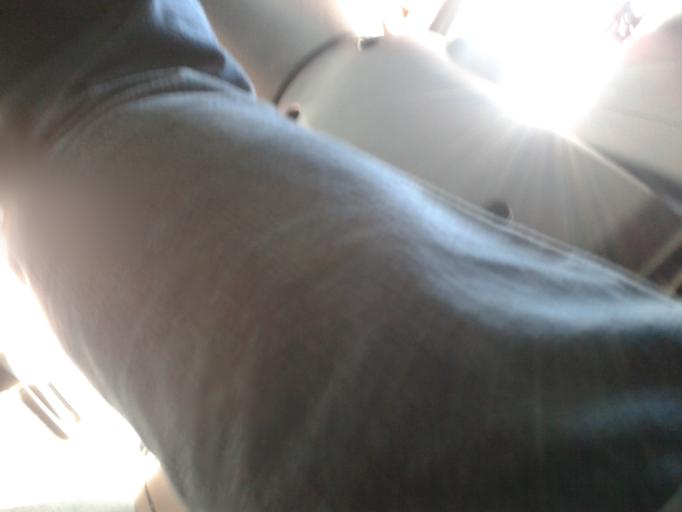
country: BR
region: Minas Gerais
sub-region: Ituiutaba
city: Ituiutaba
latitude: -19.0849
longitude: -49.7382
